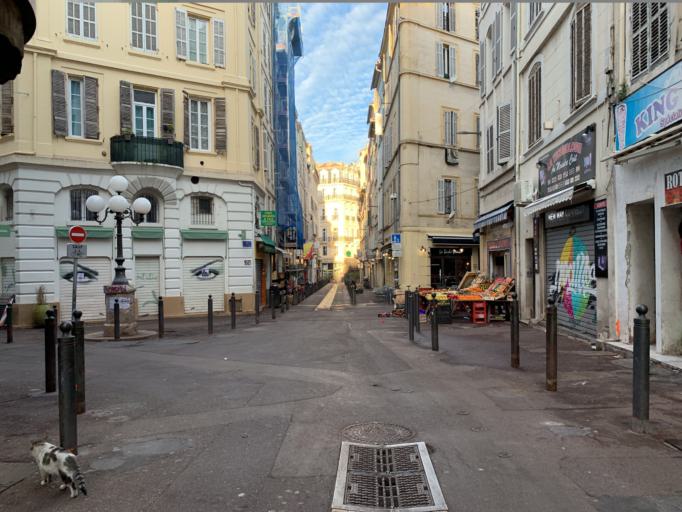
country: FR
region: Provence-Alpes-Cote d'Azur
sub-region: Departement des Bouches-du-Rhone
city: Marseille
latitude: 43.2954
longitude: 5.3796
